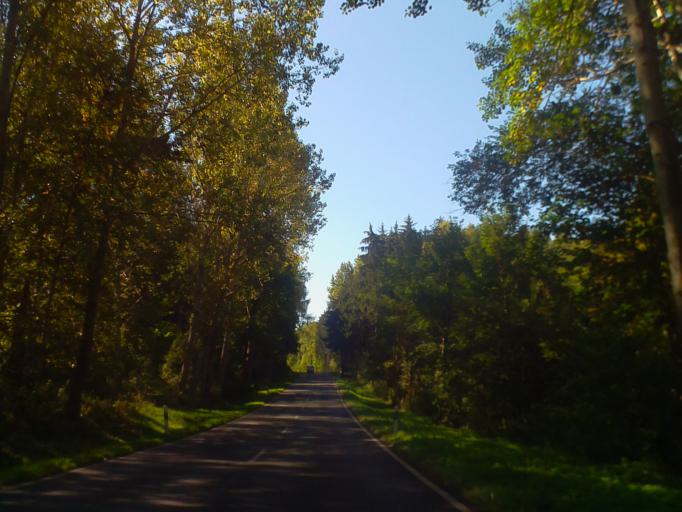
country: DE
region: Thuringia
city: Tautendorf
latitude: 50.8122
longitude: 11.9120
